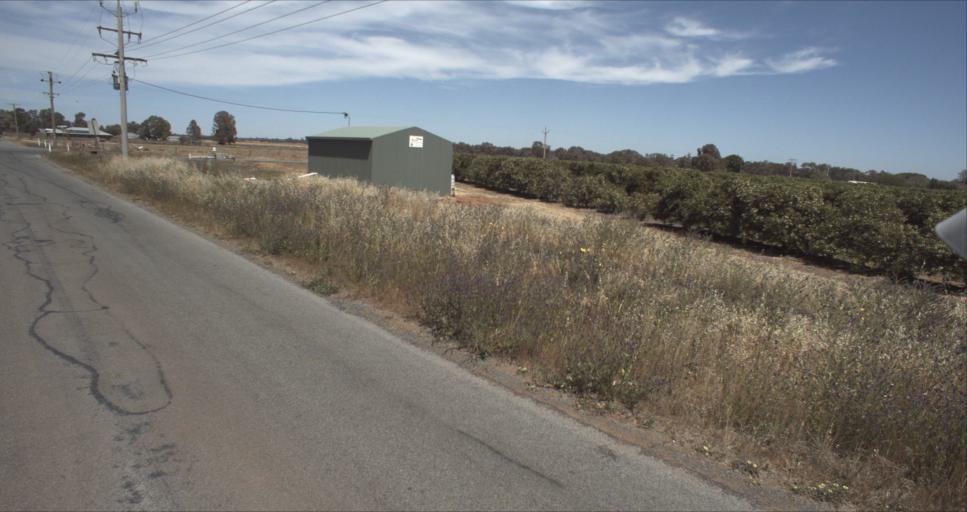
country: AU
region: New South Wales
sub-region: Leeton
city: Leeton
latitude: -34.5851
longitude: 146.4271
